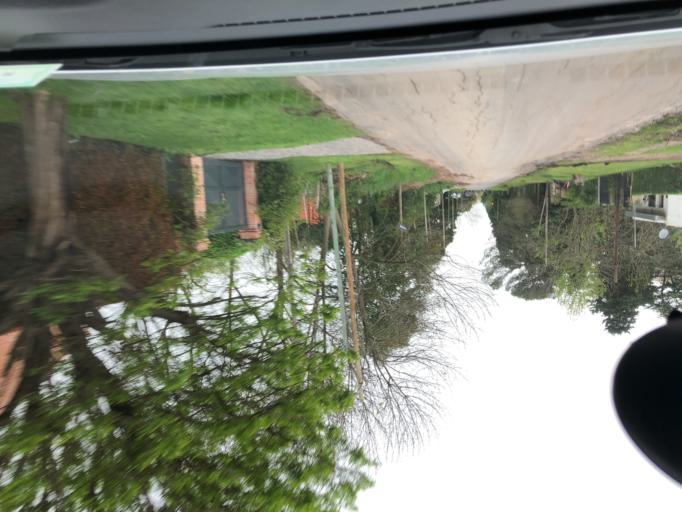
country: AR
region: Buenos Aires
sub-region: Partido de La Plata
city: La Plata
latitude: -34.8904
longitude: -58.0626
